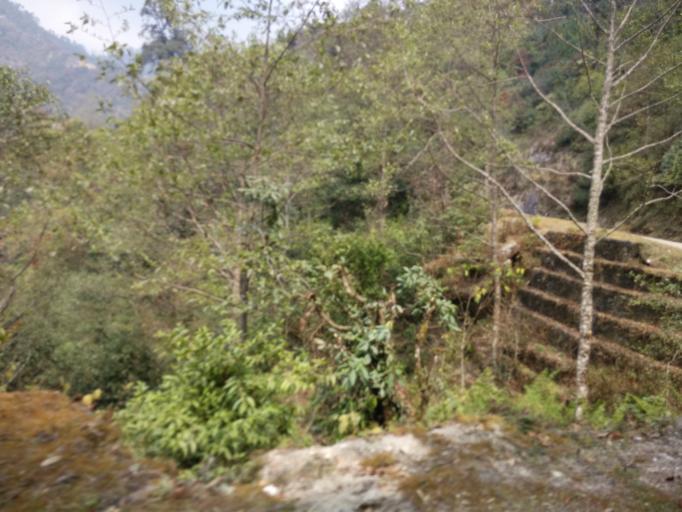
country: NP
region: Central Region
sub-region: Narayani Zone
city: Hitura
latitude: 27.5686
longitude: 85.0743
